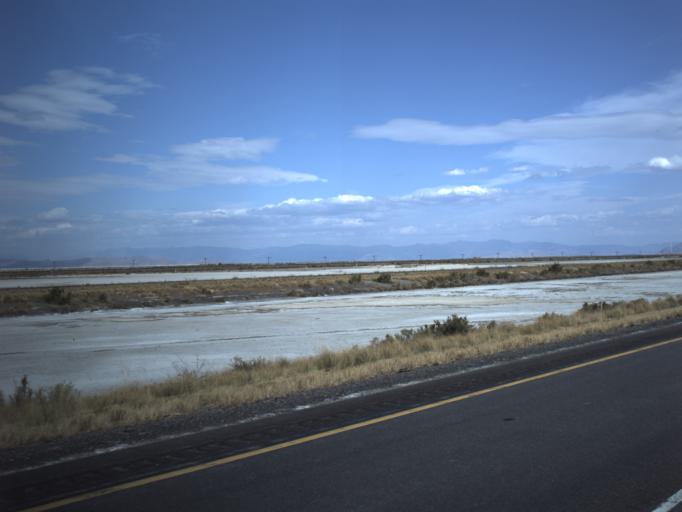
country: US
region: Utah
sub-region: Tooele County
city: Grantsville
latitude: 40.7040
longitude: -112.5086
